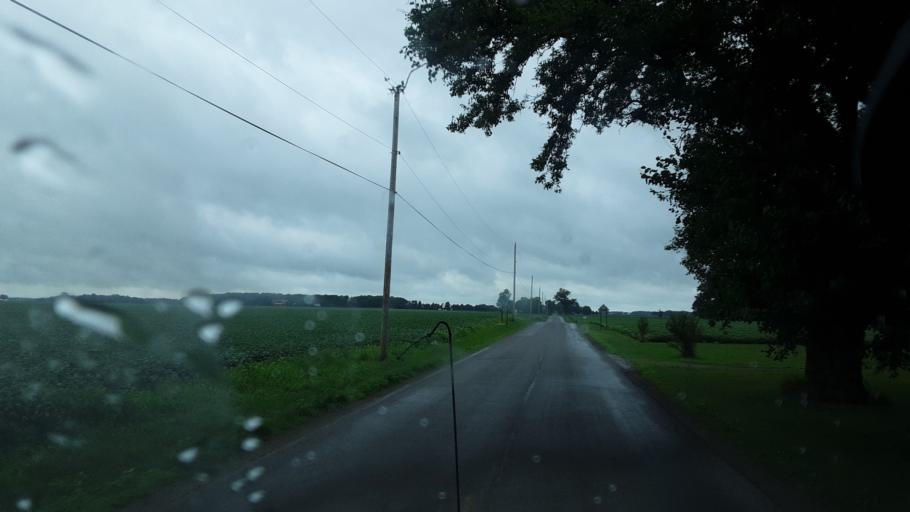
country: US
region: Ohio
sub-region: Van Wert County
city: Van Wert
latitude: 40.8006
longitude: -84.6149
